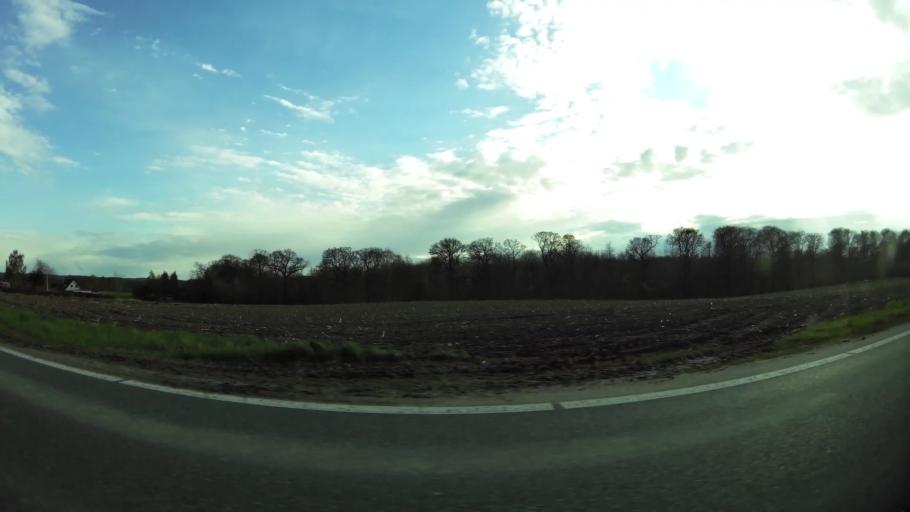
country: DK
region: Central Jutland
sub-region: Syddjurs Kommune
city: Hornslet
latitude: 56.3587
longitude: 10.3378
